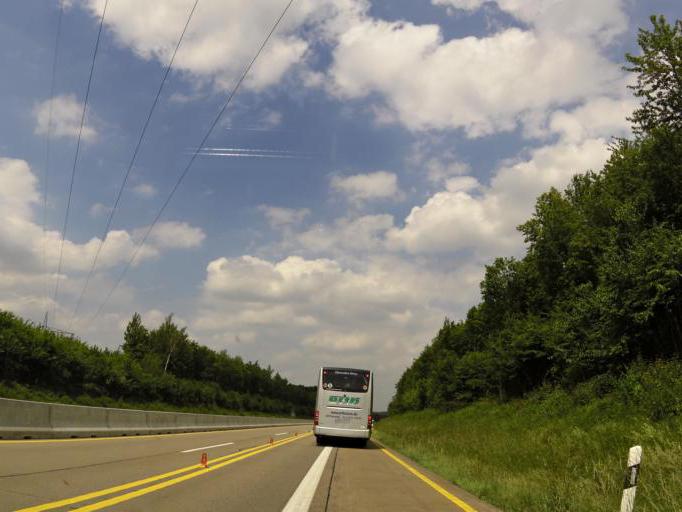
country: DE
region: Bavaria
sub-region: Regierungsbezirk Mittelfranken
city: Gollhofen
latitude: 49.5531
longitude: 10.1634
